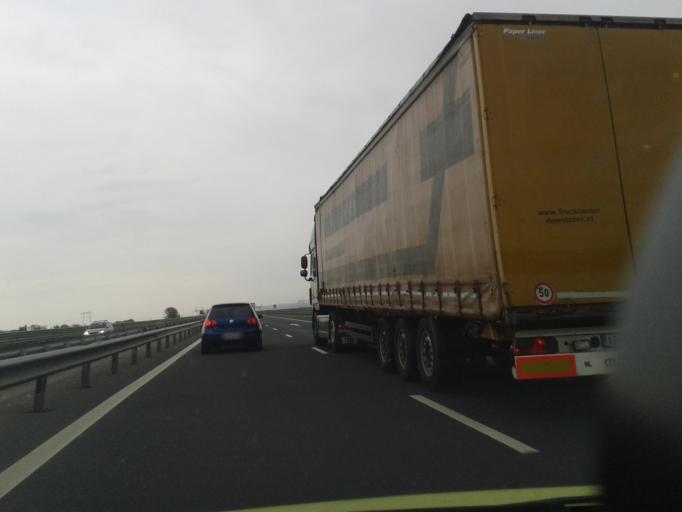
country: RO
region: Hunedoara
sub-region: Comuna Turdas
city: Pricaz
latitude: 45.8777
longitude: 23.1919
